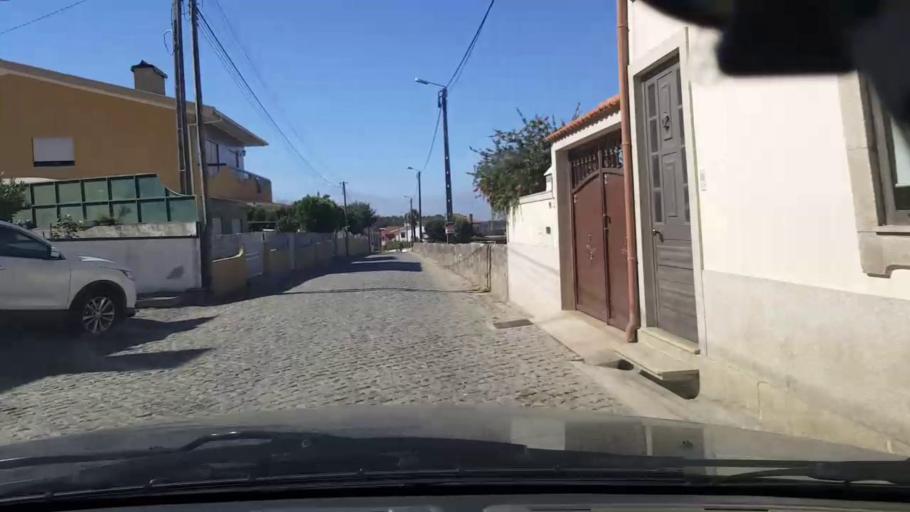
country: PT
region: Porto
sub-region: Maia
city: Gemunde
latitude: 41.2824
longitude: -8.6575
